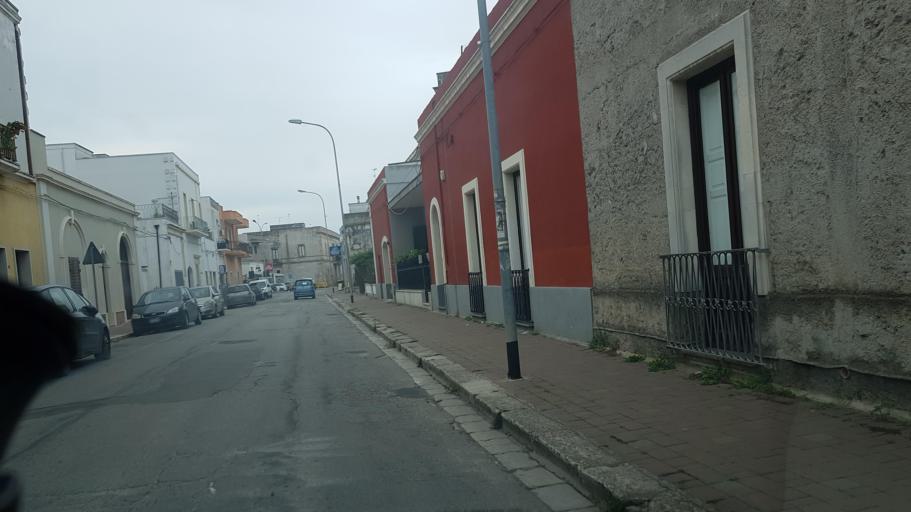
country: IT
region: Apulia
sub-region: Provincia di Lecce
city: Leverano
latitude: 40.2924
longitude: 17.9982
